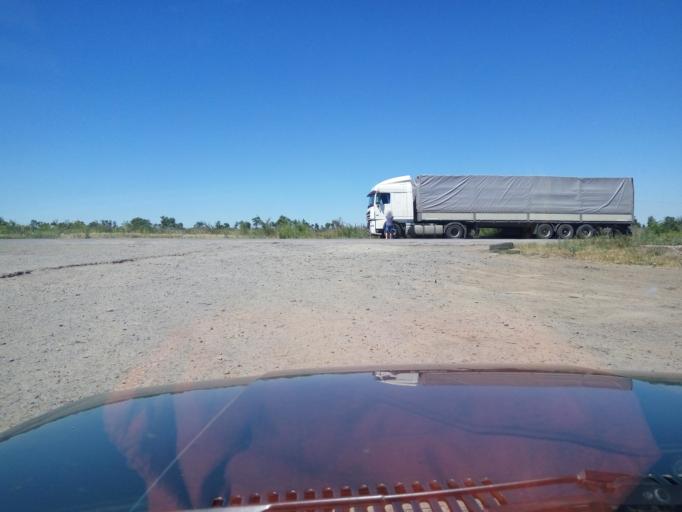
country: RU
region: Rostov
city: Bataysk
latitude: 47.0823
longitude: 39.7442
